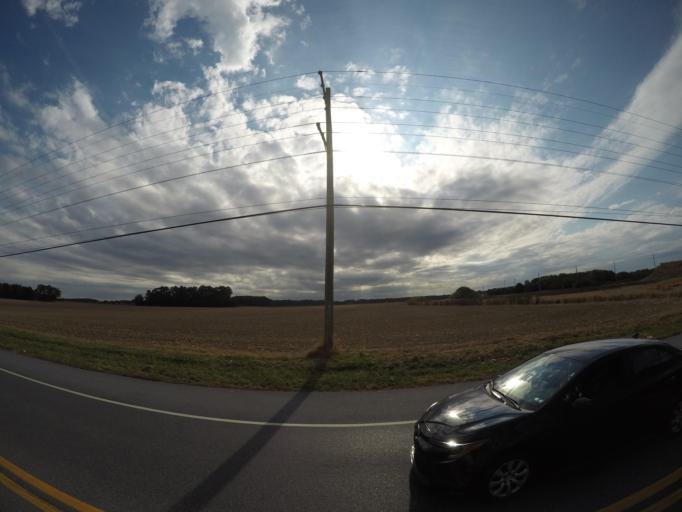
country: US
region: Delaware
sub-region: Sussex County
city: Lewes
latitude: 38.7308
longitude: -75.1506
